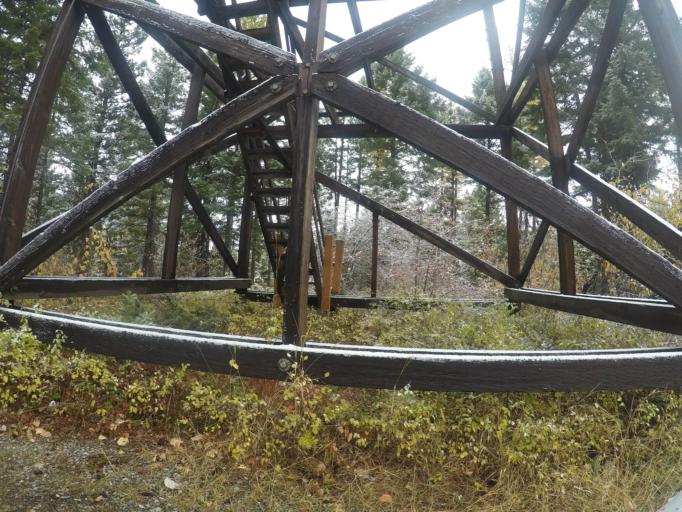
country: US
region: Montana
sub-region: Flathead County
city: Bigfork
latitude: 47.8938
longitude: -113.8745
